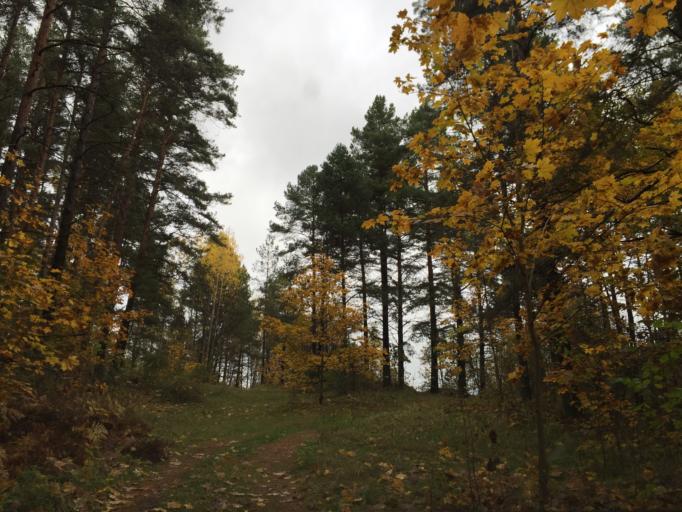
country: LV
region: Ogre
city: Ogre
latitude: 56.7971
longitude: 24.6430
